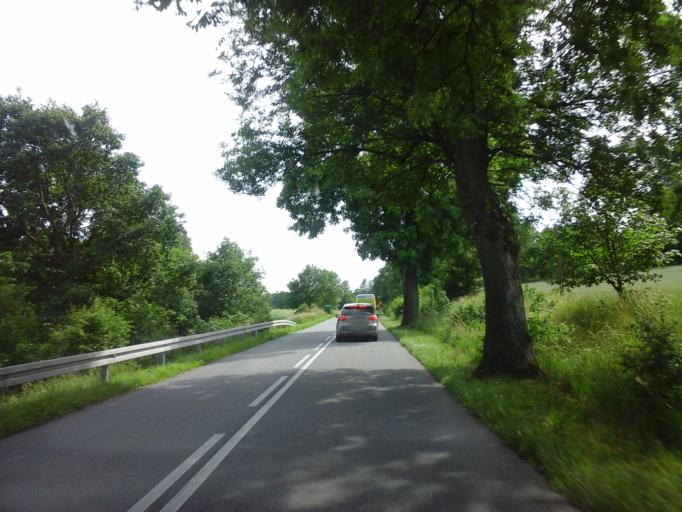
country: PL
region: West Pomeranian Voivodeship
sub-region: Powiat lobeski
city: Wegorzyno
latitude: 53.5723
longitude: 15.5870
